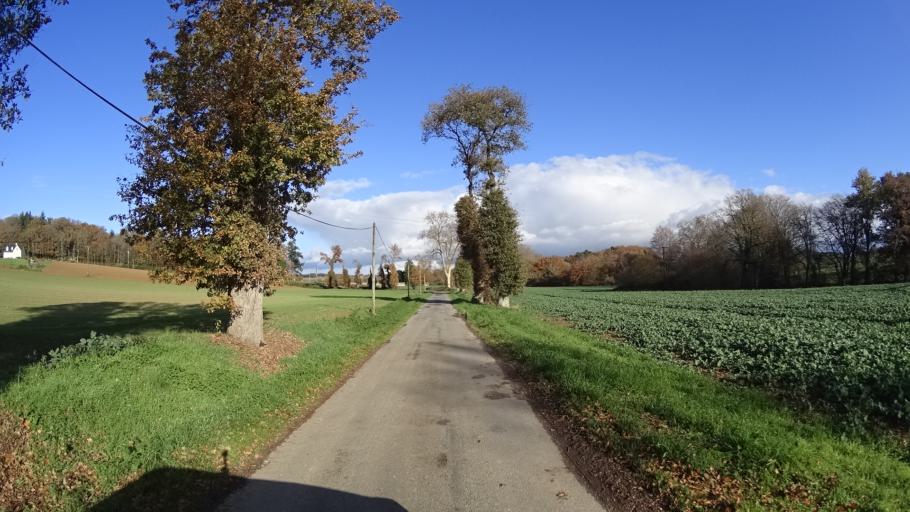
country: FR
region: Brittany
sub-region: Departement d'Ille-et-Vilaine
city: Sixt-sur-Aff
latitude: 47.8323
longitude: -2.0776
